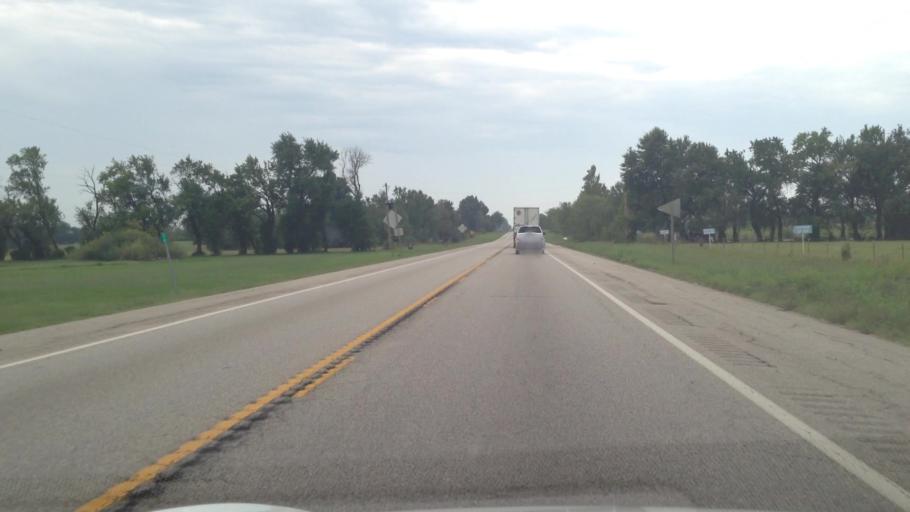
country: US
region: Kansas
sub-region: Crawford County
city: Pittsburg
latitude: 37.3326
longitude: -94.7054
